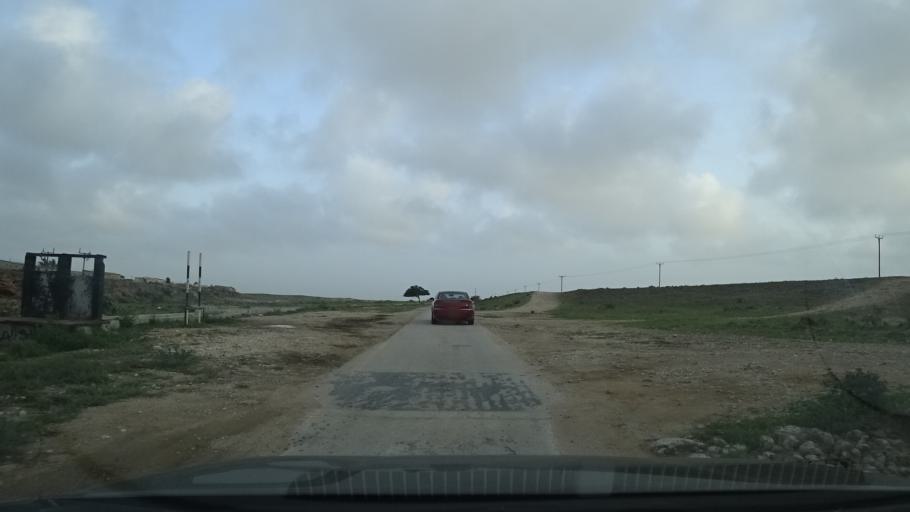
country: OM
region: Zufar
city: Salalah
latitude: 17.0995
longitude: 54.2332
